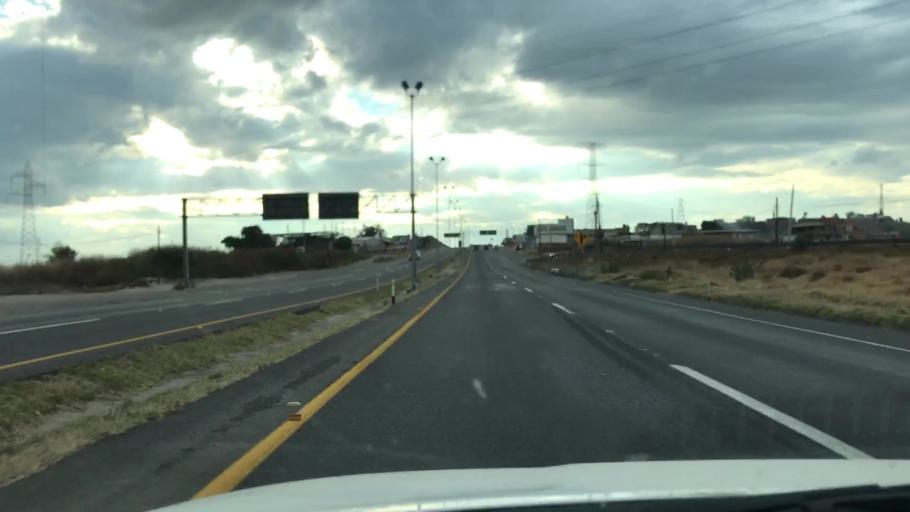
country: MX
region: Guanajuato
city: Penjamo
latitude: 20.4207
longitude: -101.7177
